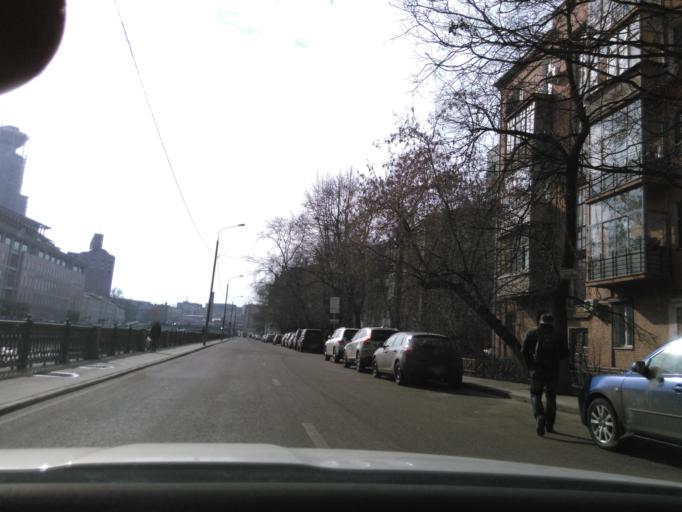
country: RU
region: Moscow
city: Zamoskvorech'ye
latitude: 55.7366
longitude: 37.6395
